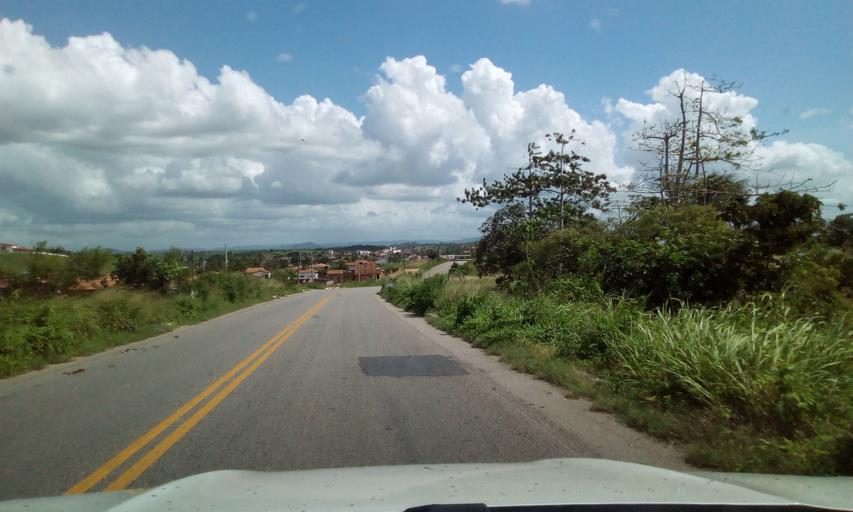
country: BR
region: Paraiba
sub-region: Guarabira
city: Guarabira
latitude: -6.8491
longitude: -35.3669
